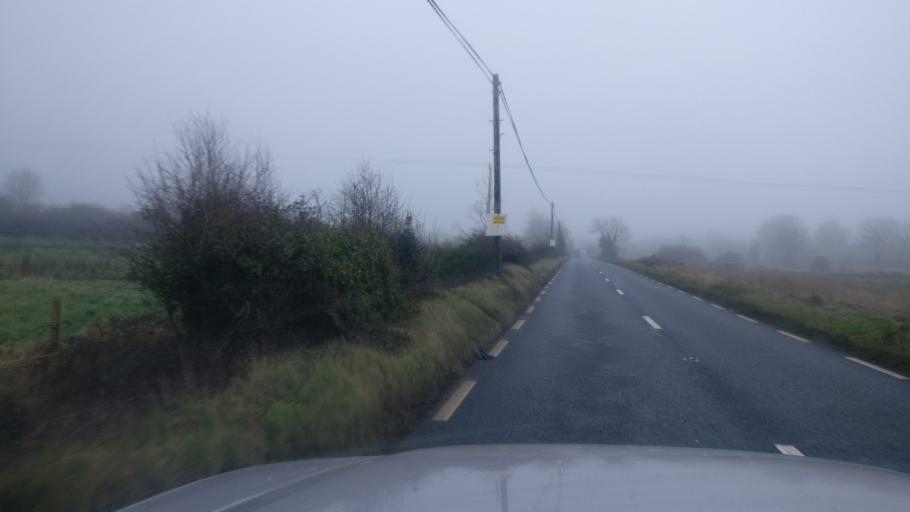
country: IE
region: Connaught
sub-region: County Galway
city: Loughrea
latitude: 53.1865
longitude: -8.6198
